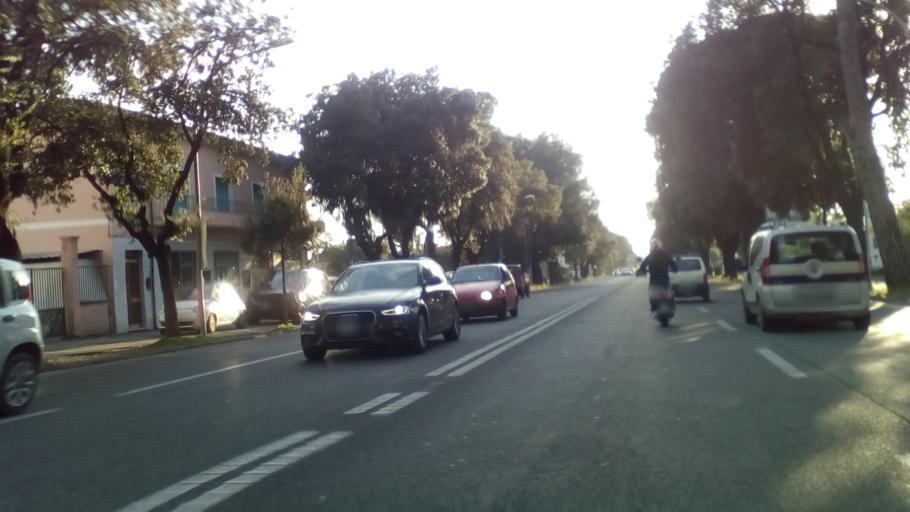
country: IT
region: Tuscany
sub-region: Provincia di Massa-Carrara
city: Carrara
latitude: 44.0585
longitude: 10.0661
